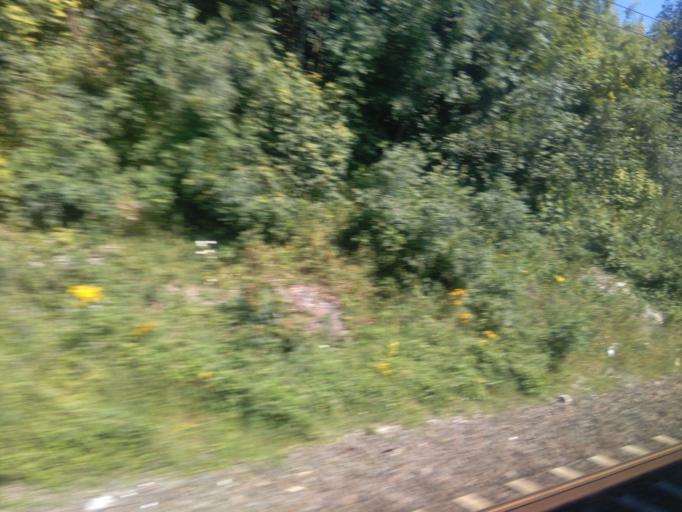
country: GB
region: England
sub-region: Luton
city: Luton
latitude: 51.8621
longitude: -0.3842
